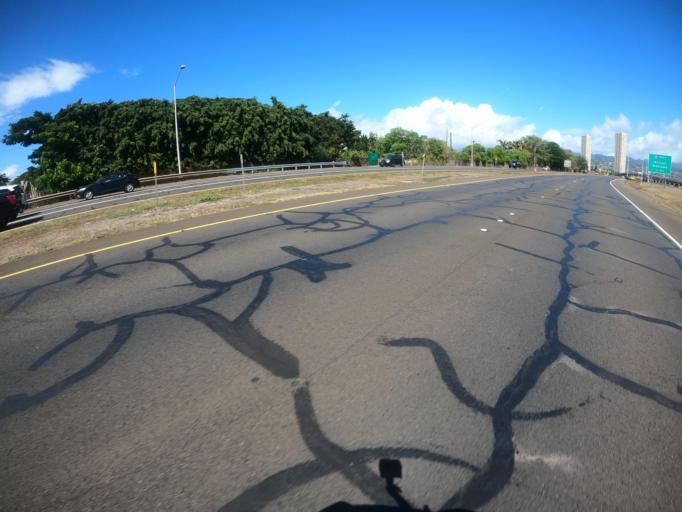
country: US
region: Hawaii
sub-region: Honolulu County
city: Pearl City, Manana
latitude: 21.3953
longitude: -157.9871
